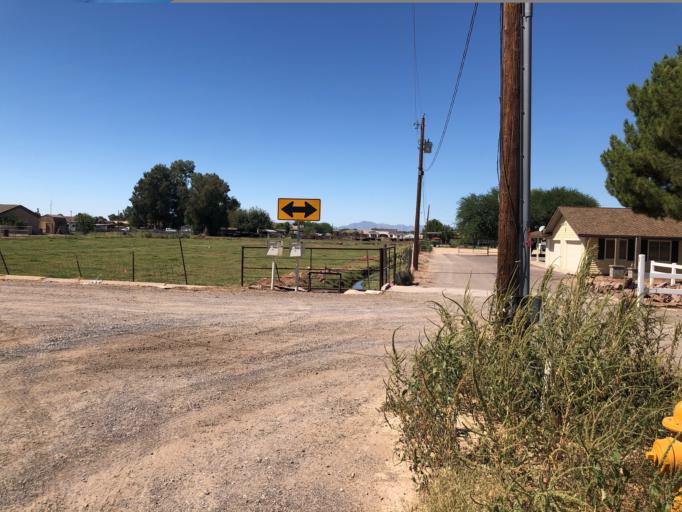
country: US
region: Arizona
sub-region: Maricopa County
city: Sun Lakes
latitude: 33.2280
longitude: -111.8151
